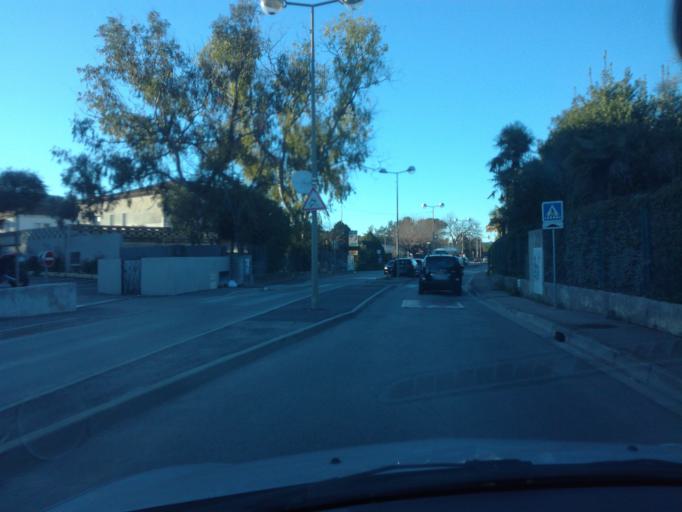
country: FR
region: Provence-Alpes-Cote d'Azur
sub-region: Departement des Alpes-Maritimes
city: Mouans-Sartoux
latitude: 43.6064
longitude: 6.9717
